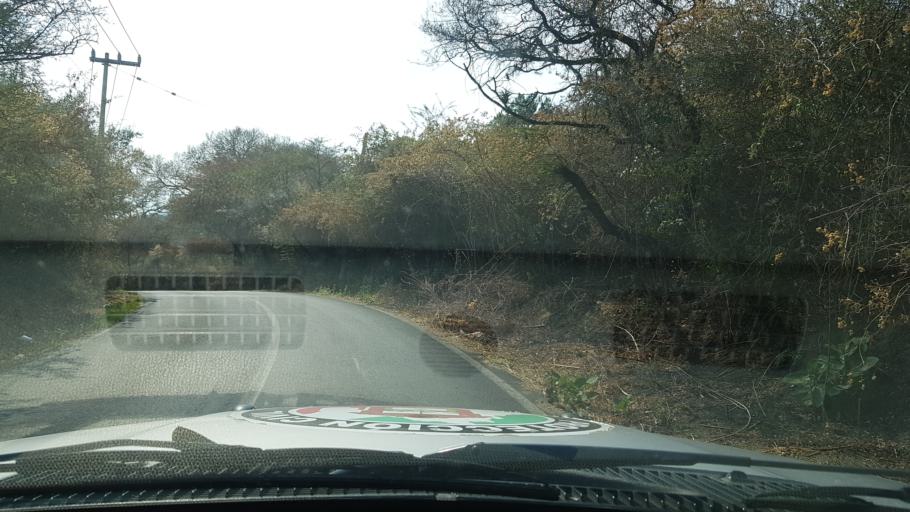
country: MX
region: Mexico
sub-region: Ozumba
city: San Jose Tlacotitlan
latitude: 18.9899
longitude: -98.8218
